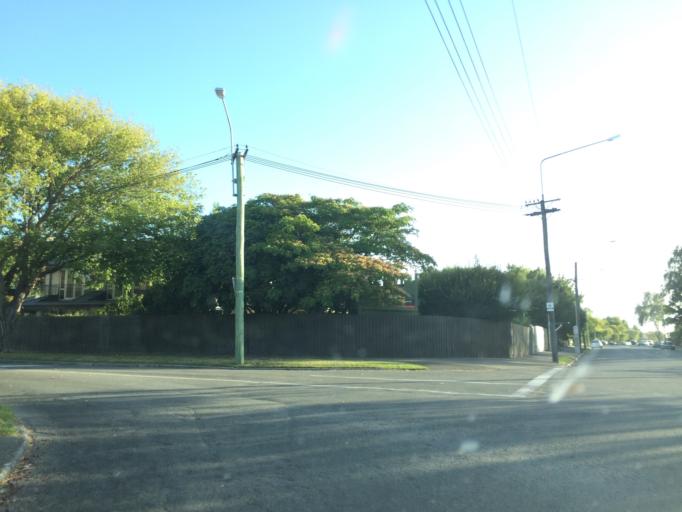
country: NZ
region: Canterbury
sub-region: Christchurch City
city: Christchurch
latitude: -43.5040
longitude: 172.5822
